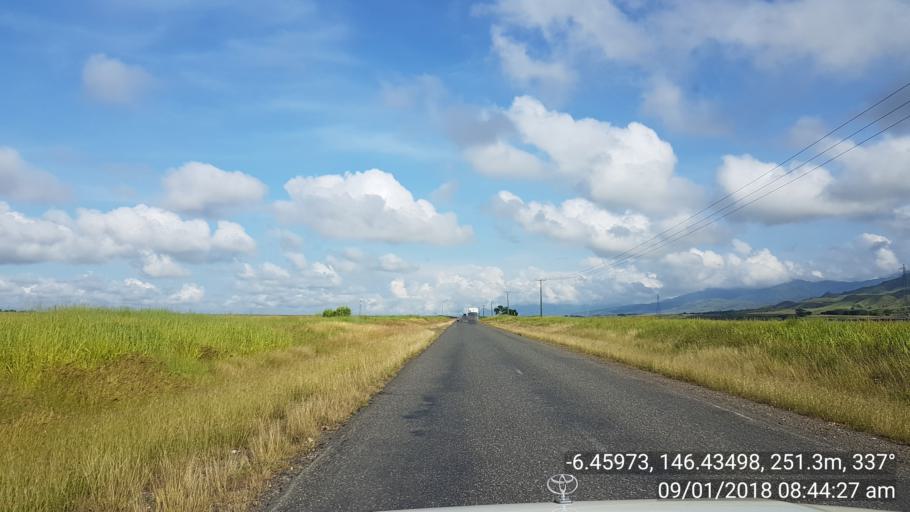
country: PG
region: Eastern Highlands
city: Kainantu
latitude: -6.4600
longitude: 146.4350
